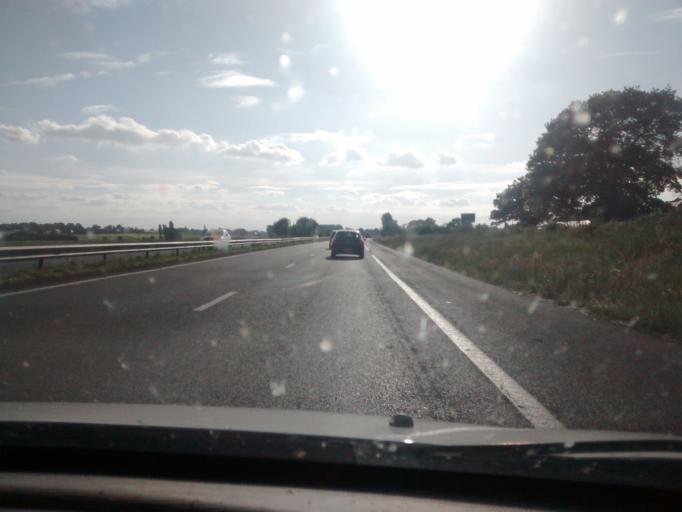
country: FR
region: Brittany
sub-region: Departement d'Ille-et-Vilaine
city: Etrelles
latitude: 48.0720
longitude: -1.2282
